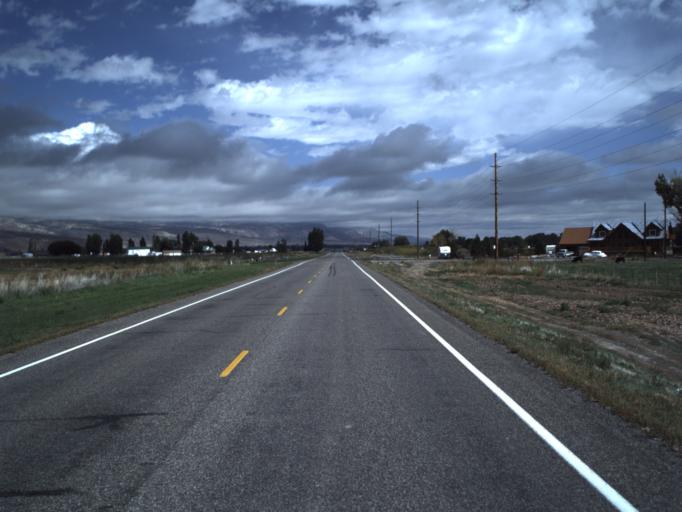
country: US
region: Utah
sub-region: Sevier County
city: Richfield
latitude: 38.7103
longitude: -112.1068
